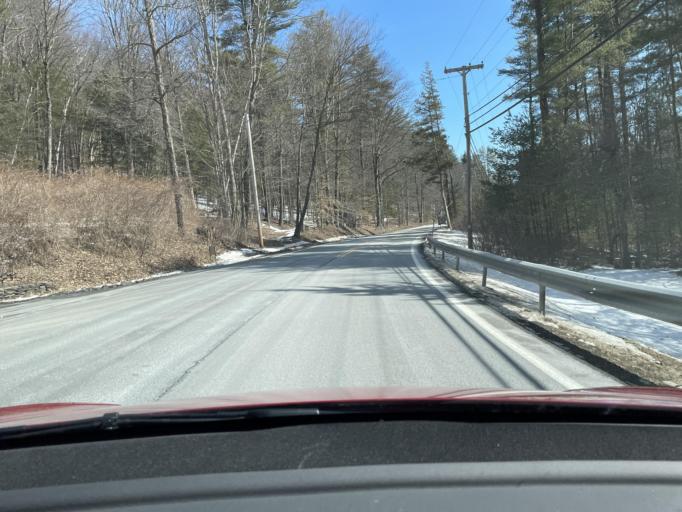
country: US
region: New York
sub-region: Ulster County
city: Woodstock
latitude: 42.0785
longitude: -74.2155
